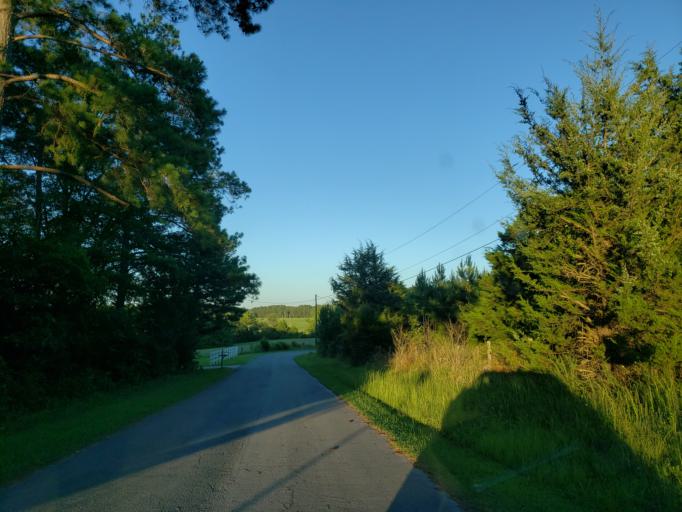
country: US
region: Georgia
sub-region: Bartow County
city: Euharlee
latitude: 34.0806
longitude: -84.9264
